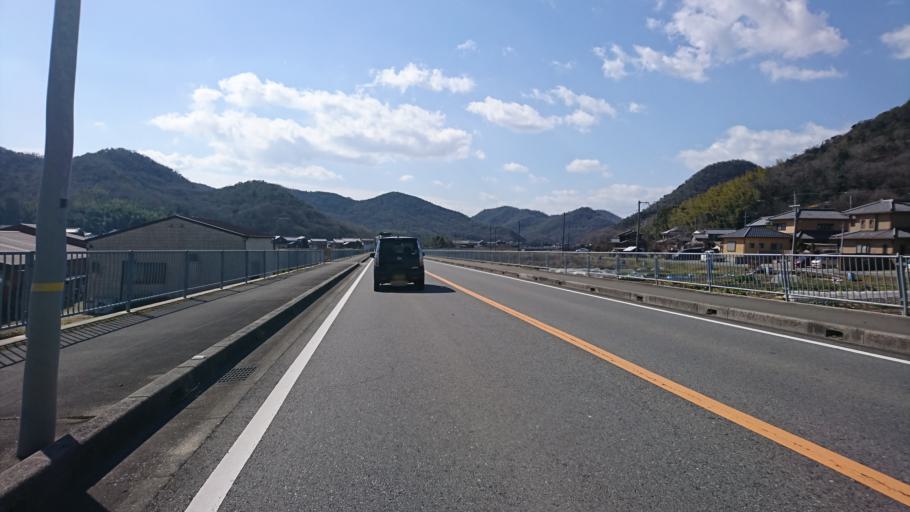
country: JP
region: Hyogo
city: Kakogawacho-honmachi
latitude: 34.8620
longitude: 134.7903
